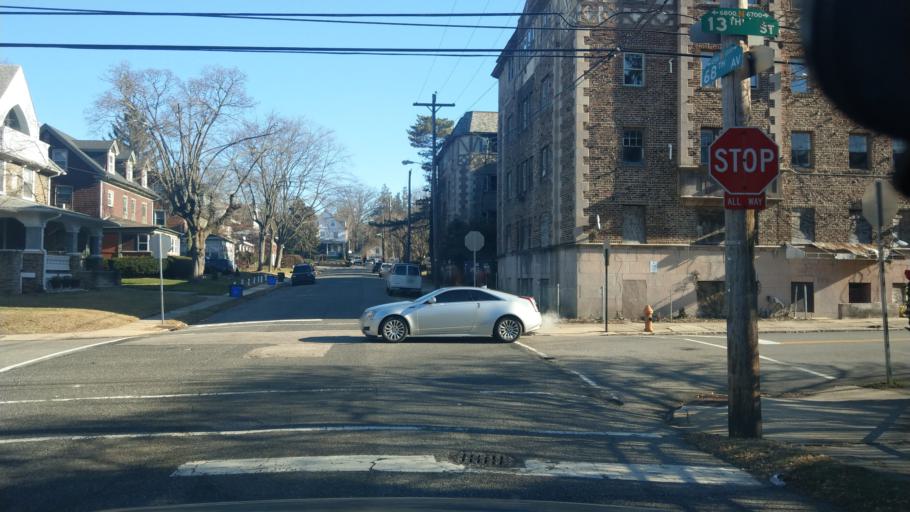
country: US
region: Pennsylvania
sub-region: Montgomery County
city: Wyncote
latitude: 40.0564
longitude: -75.1389
